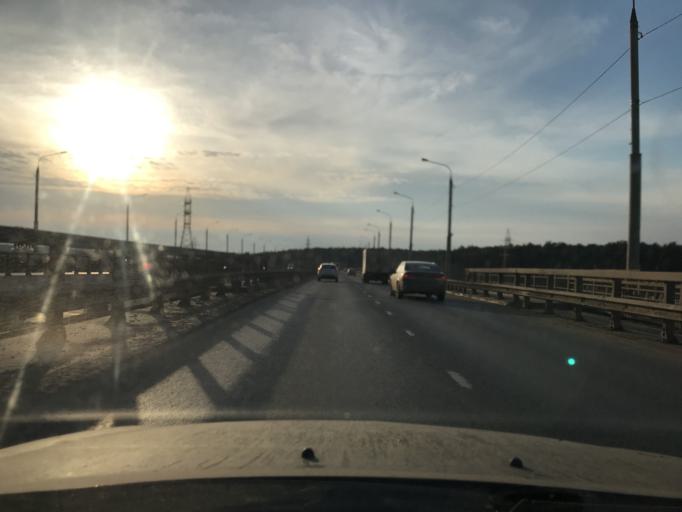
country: RU
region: Kaluga
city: Kaluga
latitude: 54.5120
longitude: 36.2162
